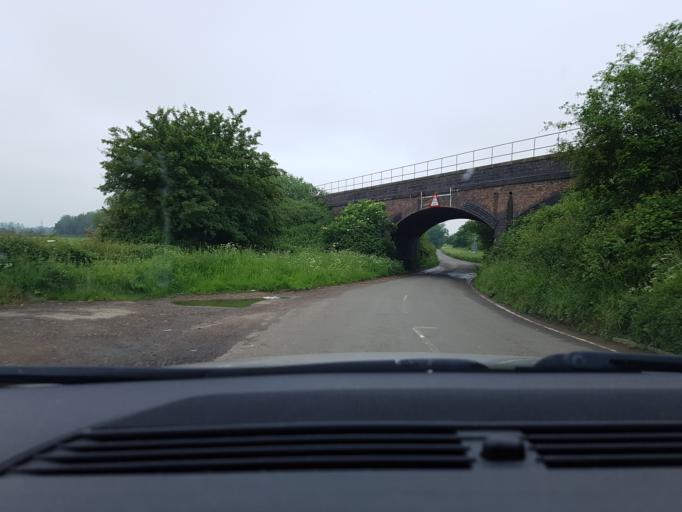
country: GB
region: England
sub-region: Buckinghamshire
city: Winslow
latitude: 51.9442
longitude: -0.9041
